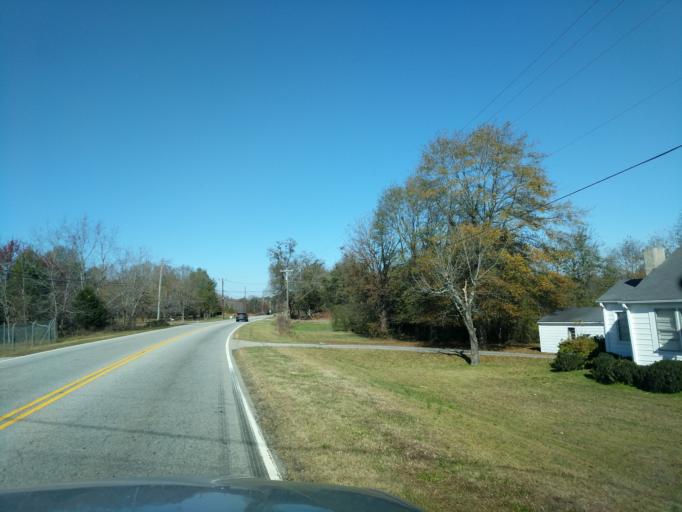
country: US
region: South Carolina
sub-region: Greenville County
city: Taylors
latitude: 34.9762
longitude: -82.3315
